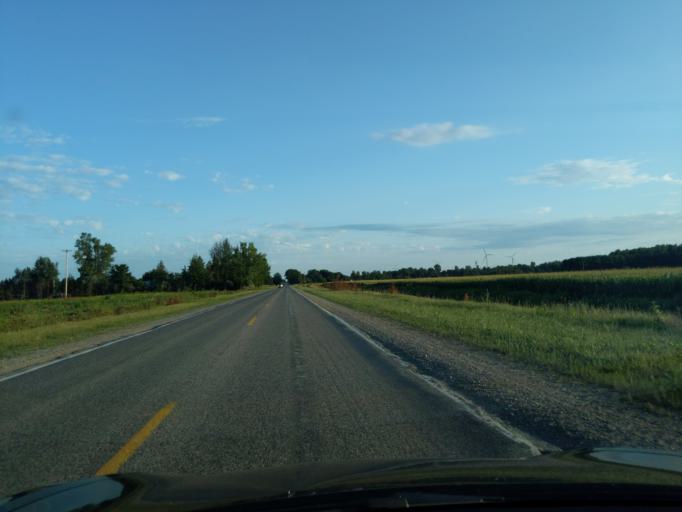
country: US
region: Michigan
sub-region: Gratiot County
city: Breckenridge
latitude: 43.4256
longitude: -84.3699
